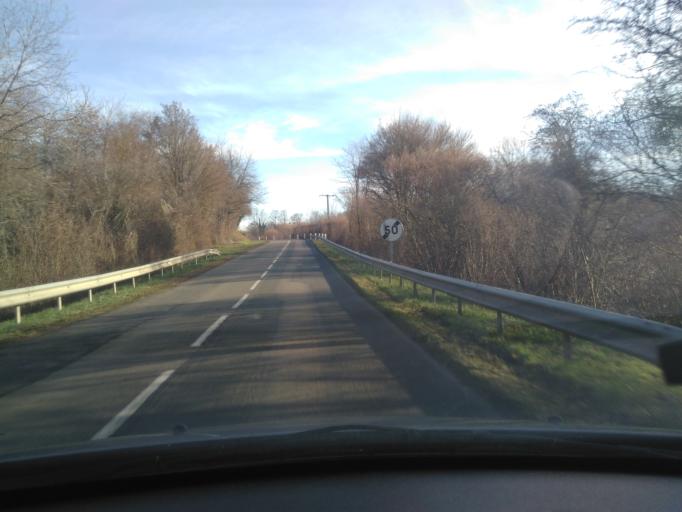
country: FR
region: Centre
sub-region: Departement du Cher
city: Le Chatelet
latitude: 46.6398
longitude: 2.3008
